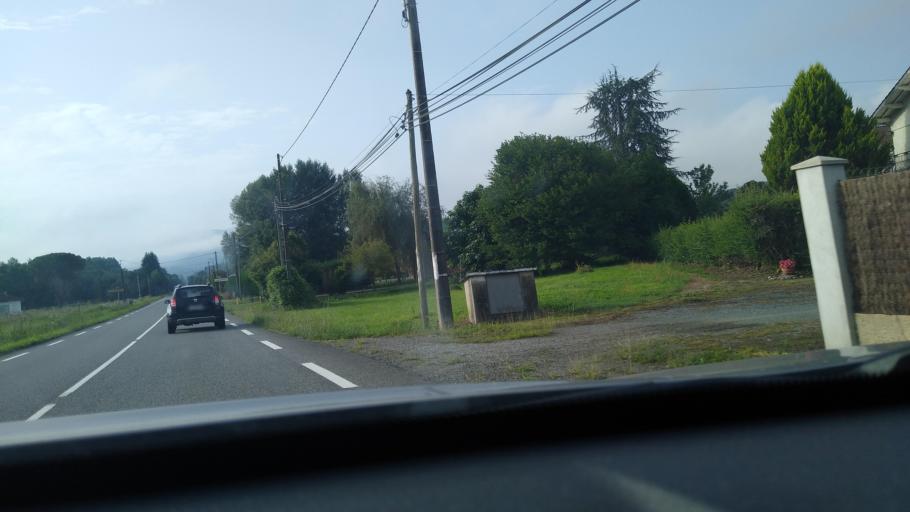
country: FR
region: Midi-Pyrenees
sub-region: Departement de la Haute-Garonne
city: Salies-du-Salat
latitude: 43.0532
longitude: 0.9811
